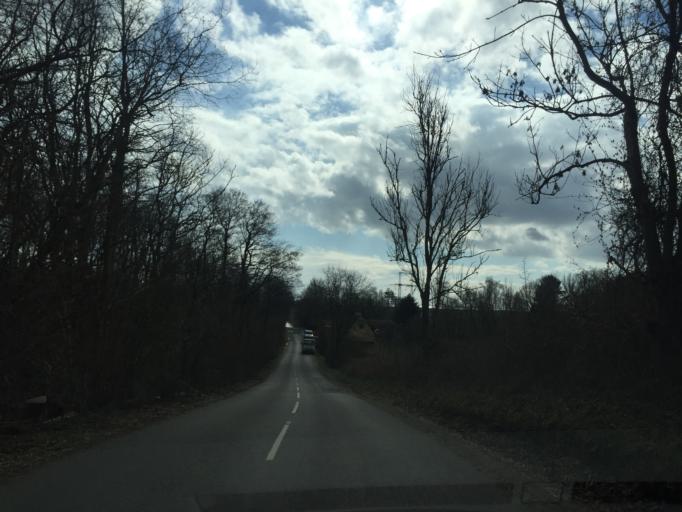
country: DK
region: South Denmark
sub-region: Svendborg Kommune
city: Svendborg
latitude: 55.0939
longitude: 10.5134
